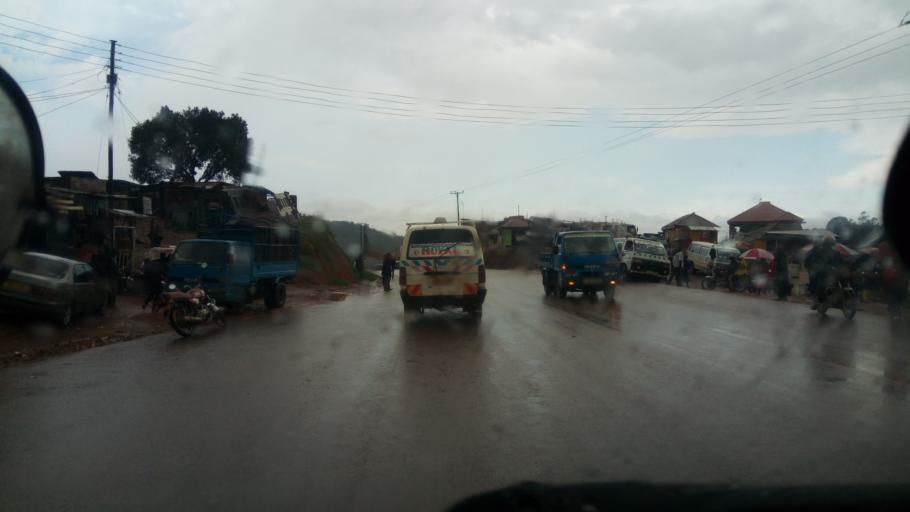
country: UG
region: Central Region
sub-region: Wakiso District
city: Wakiso
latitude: 0.3998
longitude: 32.4781
